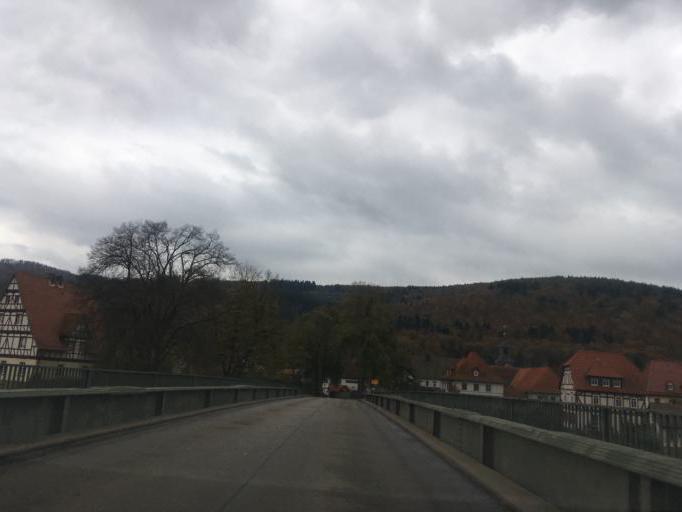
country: DE
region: Lower Saxony
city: Bodenfelde
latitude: 51.6011
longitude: 9.5516
